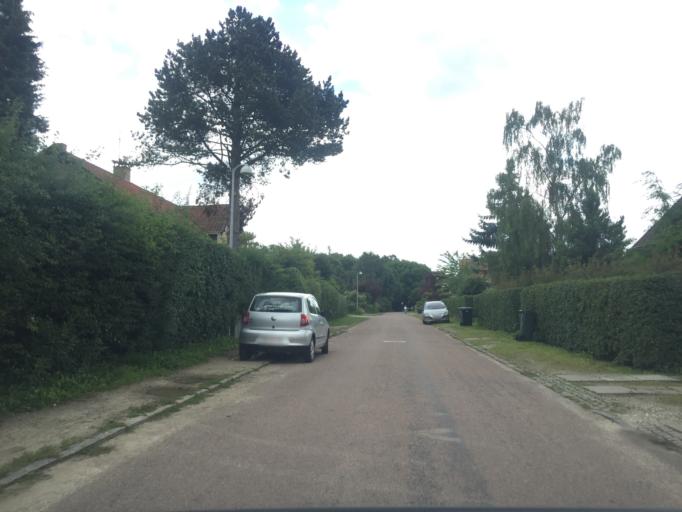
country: DK
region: Capital Region
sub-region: Lyngby-Tarbaek Kommune
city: Kongens Lyngby
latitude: 55.7643
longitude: 12.5154
